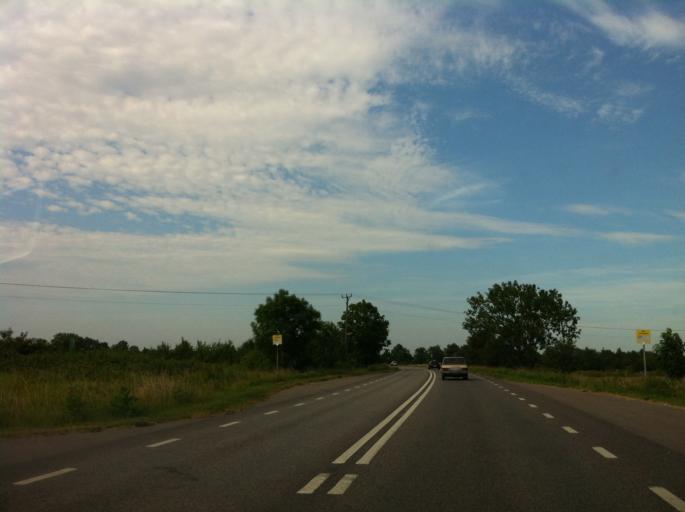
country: SE
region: Kalmar
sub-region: Borgholms Kommun
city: Borgholm
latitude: 56.8844
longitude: 16.7279
